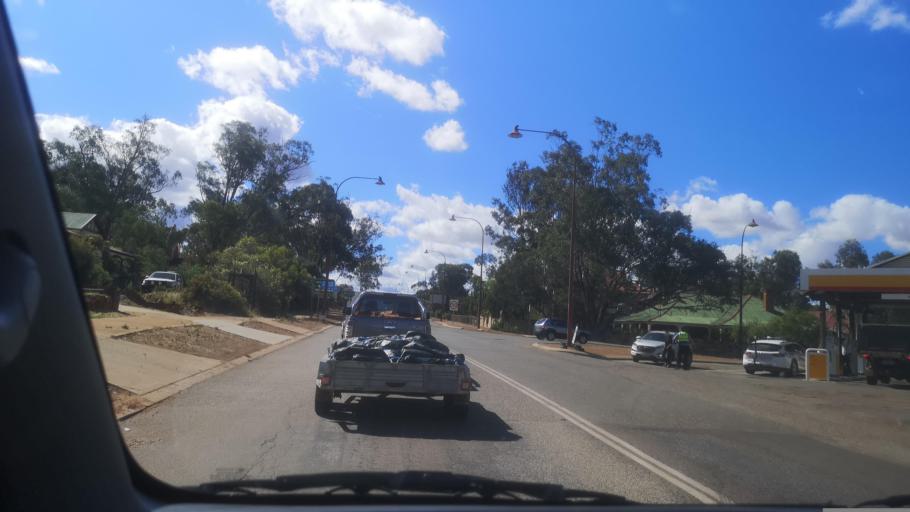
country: AU
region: Western Australia
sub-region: Toodyay
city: Toodyay
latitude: -31.5559
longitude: 116.4755
